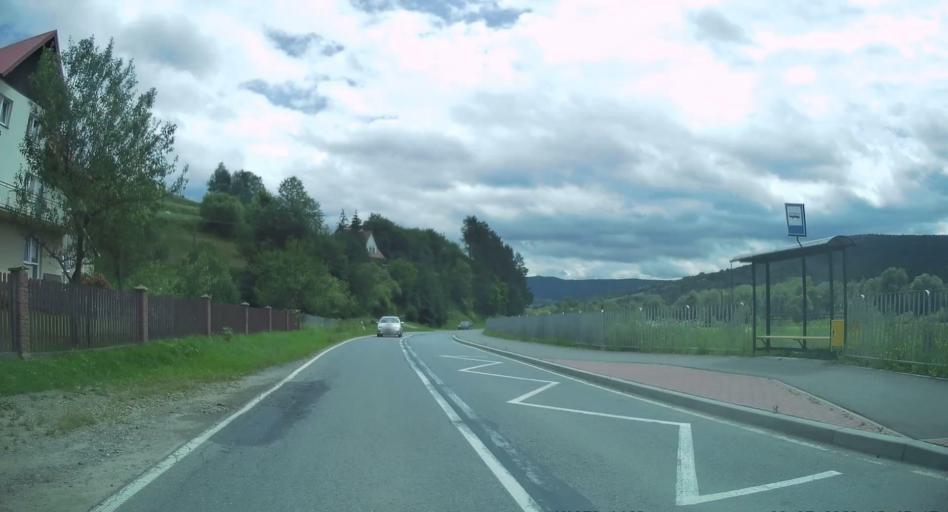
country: PL
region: Lesser Poland Voivodeship
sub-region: Powiat nowosadecki
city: Muszyna
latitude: 49.3458
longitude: 20.8175
